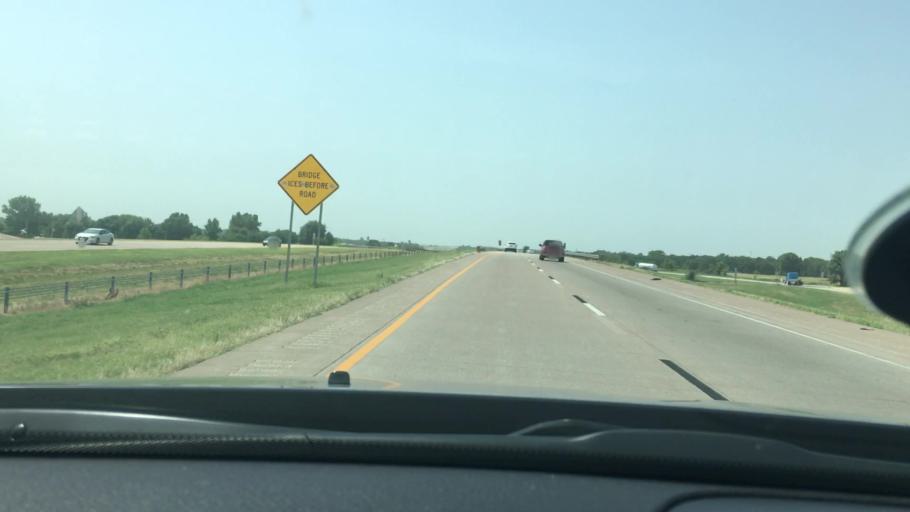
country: US
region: Oklahoma
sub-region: Garvin County
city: Wynnewood
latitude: 34.6540
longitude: -97.2207
